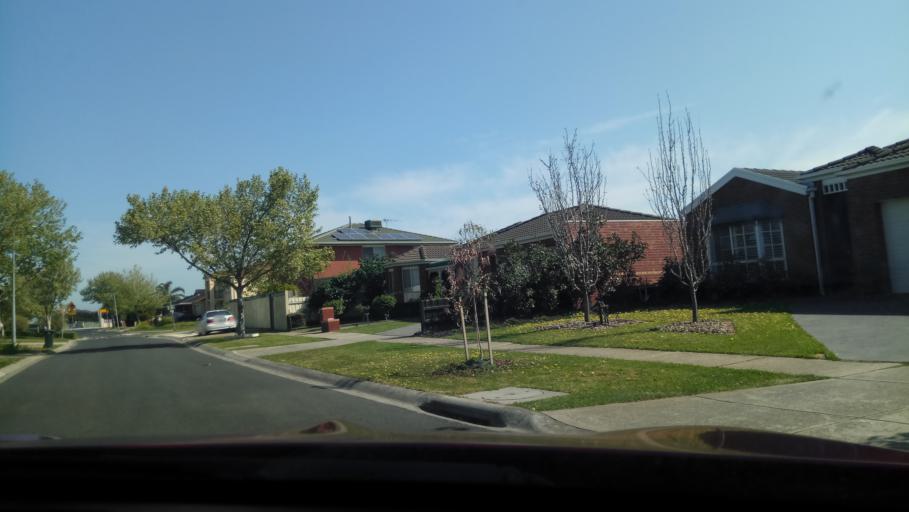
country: AU
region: Victoria
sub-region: Wyndham
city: Williams Landing
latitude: -37.8855
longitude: 144.7549
